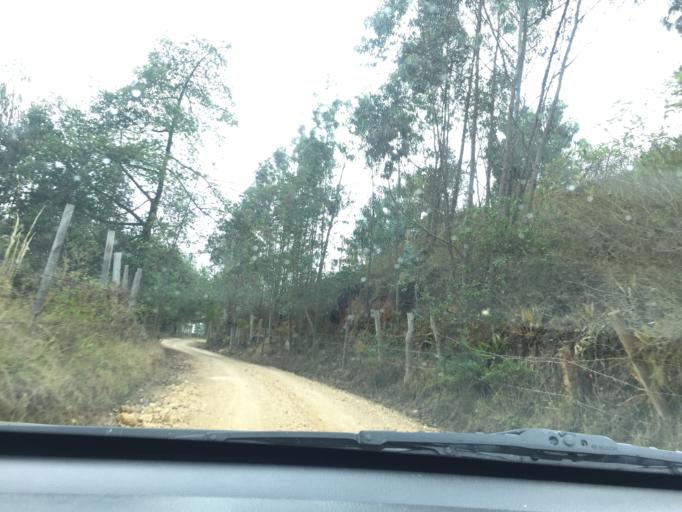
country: CO
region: Cundinamarca
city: Bojaca
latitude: 4.7104
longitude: -74.3463
